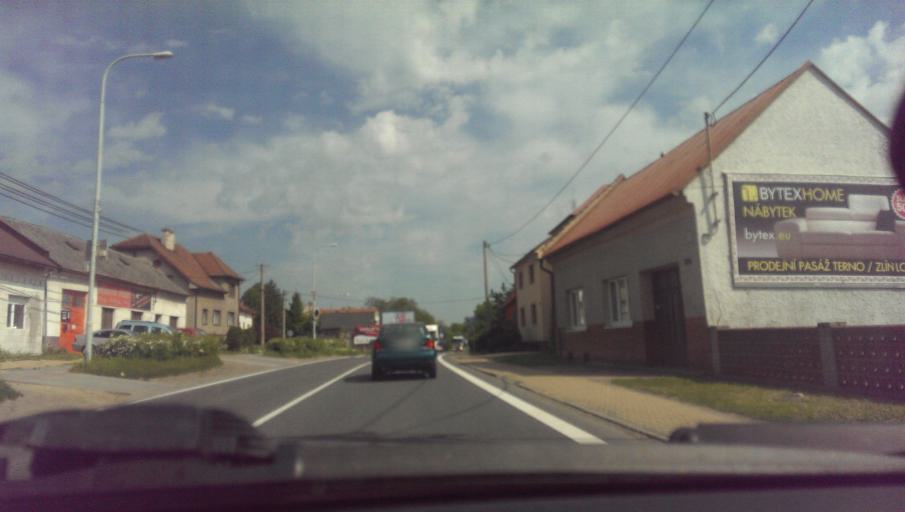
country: CZ
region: Zlin
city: Spytihnev
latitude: 49.1444
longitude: 17.4994
